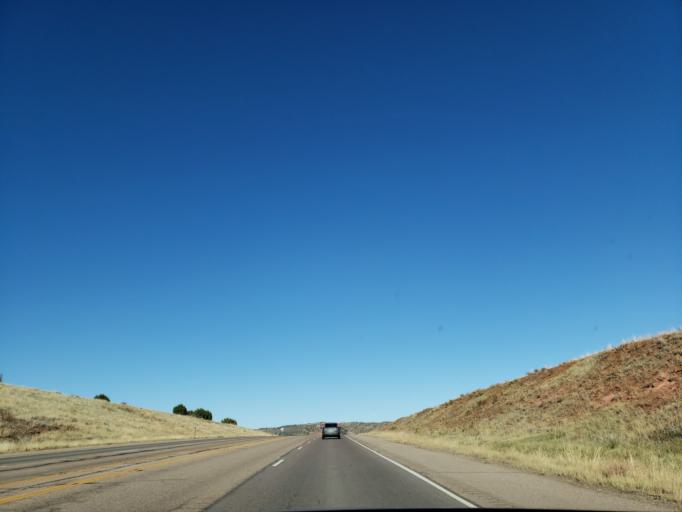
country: US
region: Colorado
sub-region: El Paso County
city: Fort Carson
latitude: 38.6135
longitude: -104.8929
